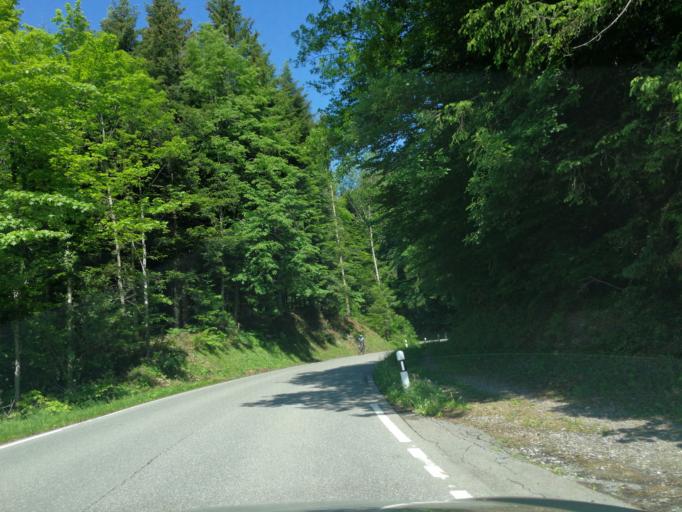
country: CH
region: Saint Gallen
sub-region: Wahlkreis See-Gaster
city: Eschenbach
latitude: 47.2267
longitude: 8.9239
